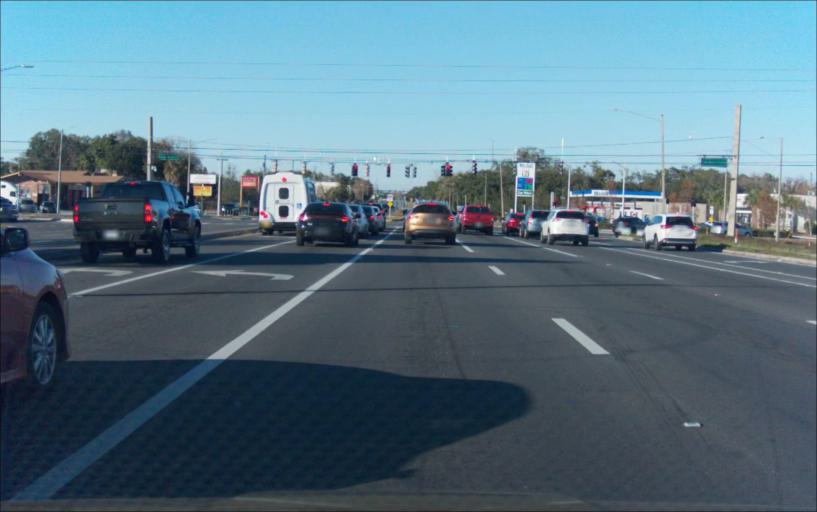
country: US
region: Florida
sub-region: Orange County
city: Orlovista
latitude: 28.5374
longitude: -81.4581
